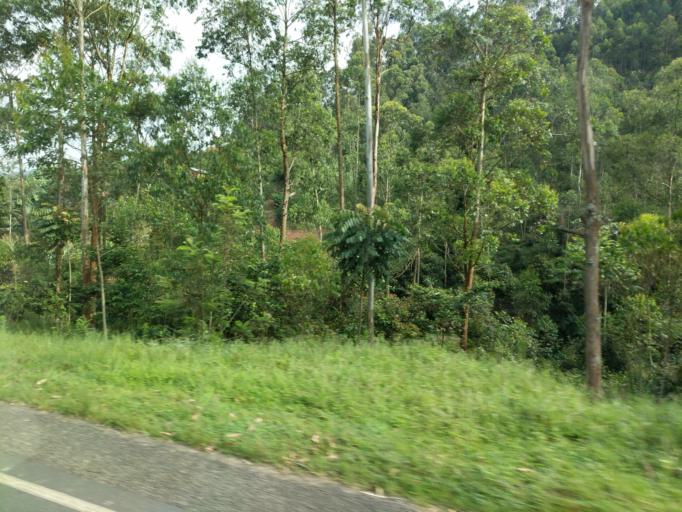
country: RW
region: Northern Province
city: Musanze
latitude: -1.6566
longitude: 29.8108
